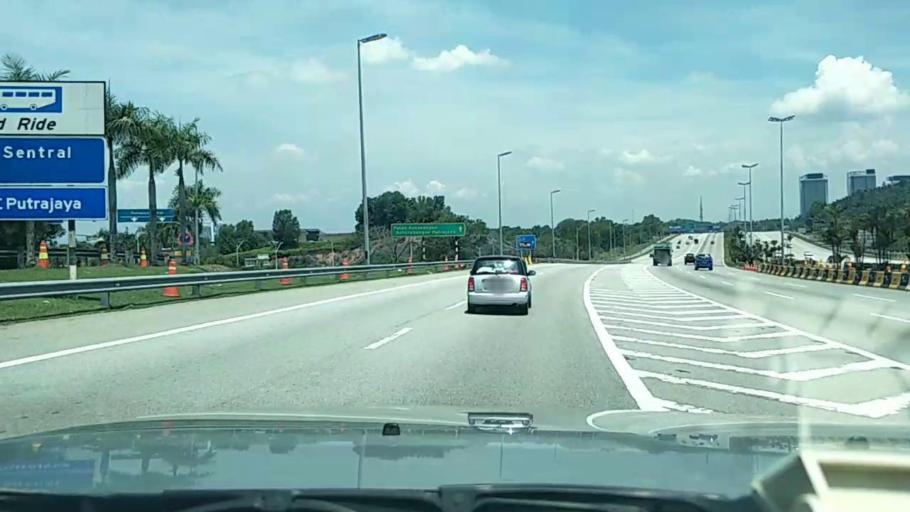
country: MY
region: Putrajaya
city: Putrajaya
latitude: 2.9372
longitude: 101.6687
